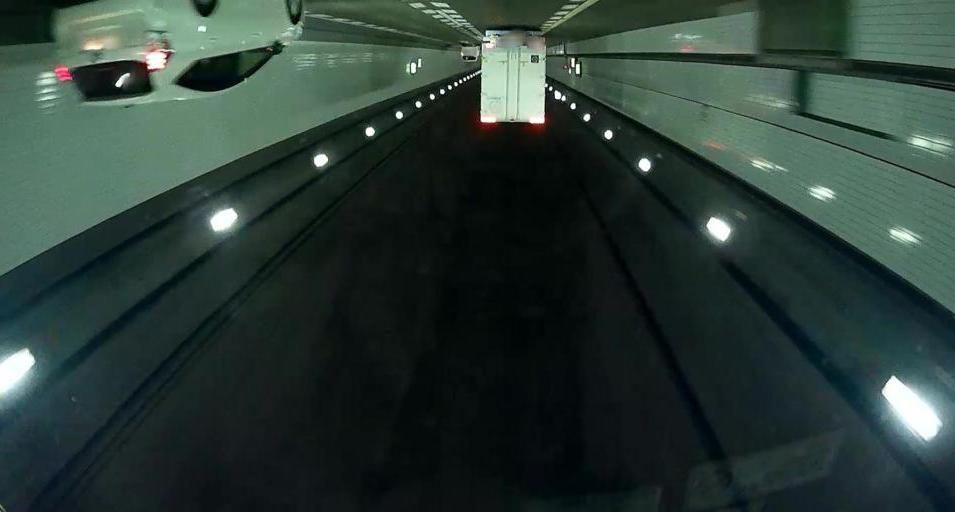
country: JP
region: Chiba
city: Kisarazu
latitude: 35.4661
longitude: 139.8715
